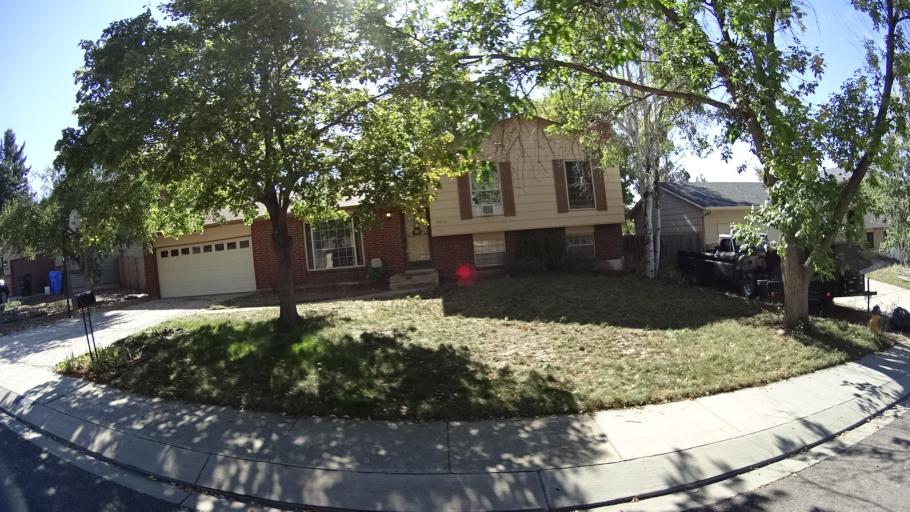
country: US
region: Colorado
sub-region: El Paso County
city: Cimarron Hills
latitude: 38.9164
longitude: -104.7700
